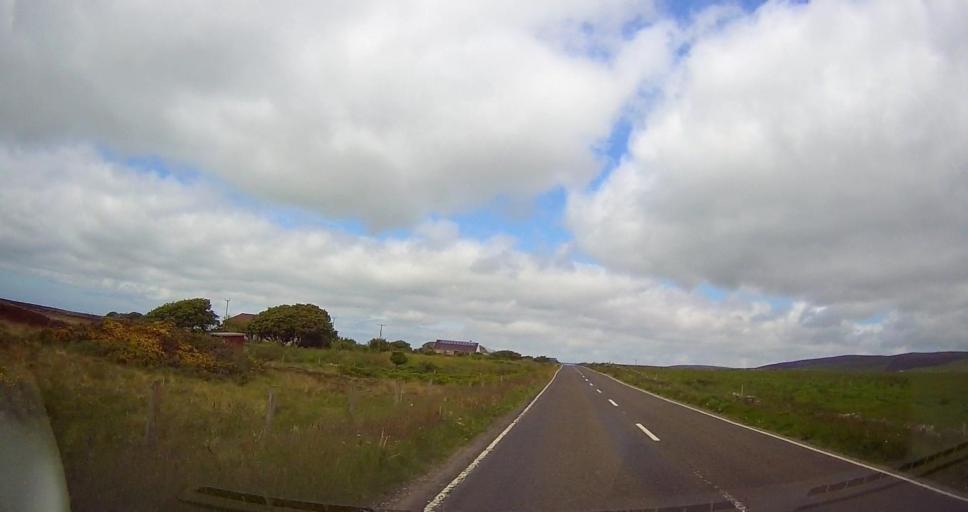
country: GB
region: Scotland
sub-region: Orkney Islands
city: Stromness
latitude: 59.0076
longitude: -3.1554
